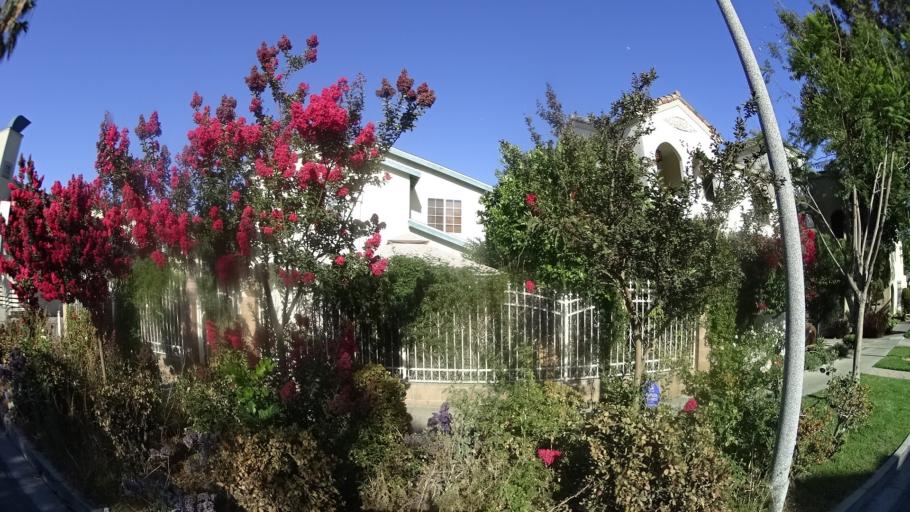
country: US
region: California
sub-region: Los Angeles County
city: Hollywood
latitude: 34.0830
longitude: -118.3196
